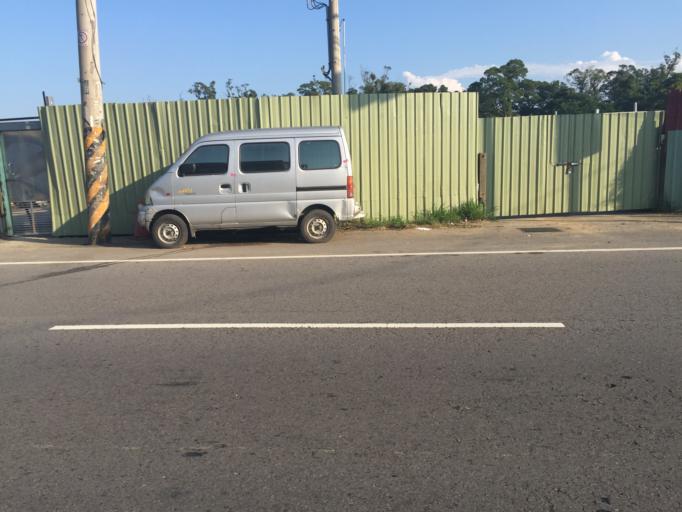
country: TW
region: Taiwan
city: Daxi
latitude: 24.9197
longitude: 121.2548
